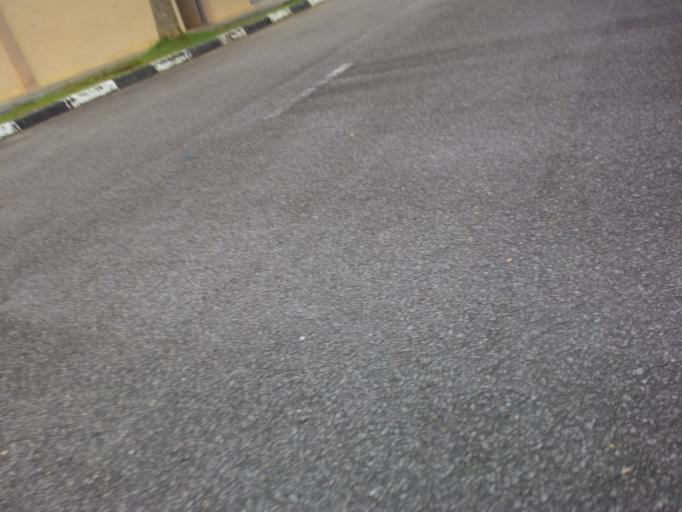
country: MY
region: Kedah
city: Kulim
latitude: 5.3837
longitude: 100.5797
